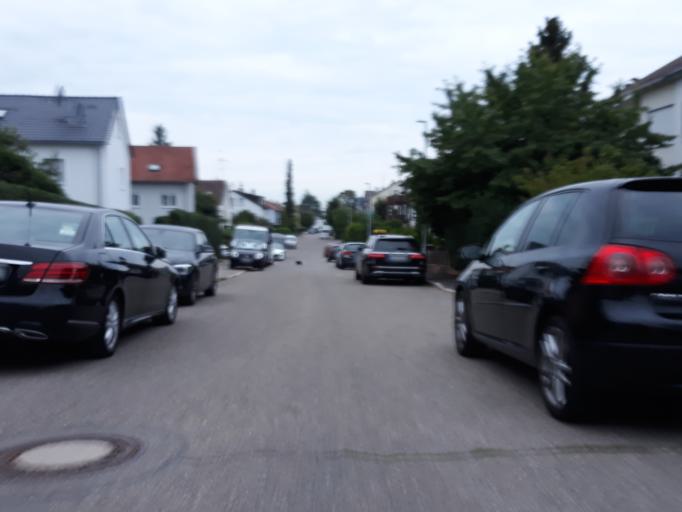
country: DE
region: Baden-Wuerttemberg
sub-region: Regierungsbezirk Stuttgart
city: Boeblingen
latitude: 48.6823
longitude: 9.0325
